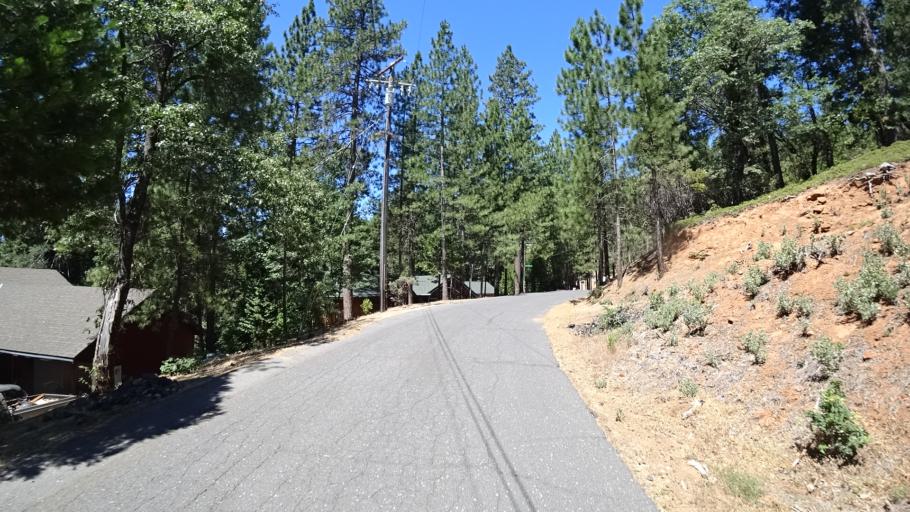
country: US
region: California
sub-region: Calaveras County
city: Arnold
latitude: 38.2377
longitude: -120.3332
